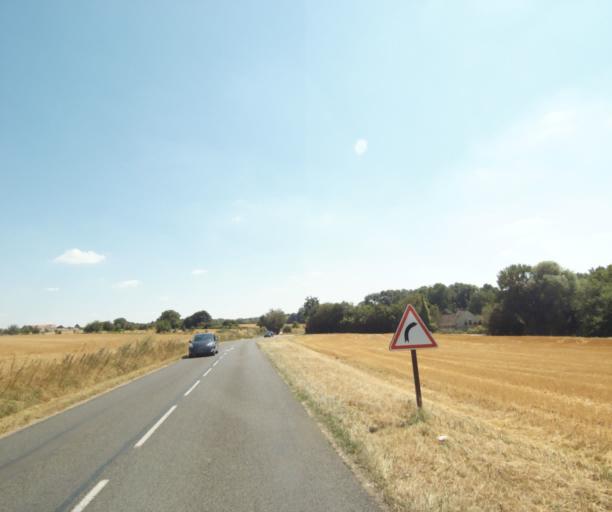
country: FR
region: Ile-de-France
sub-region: Departement de Seine-et-Marne
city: Conches-sur-Gondoire
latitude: 48.8576
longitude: 2.7282
